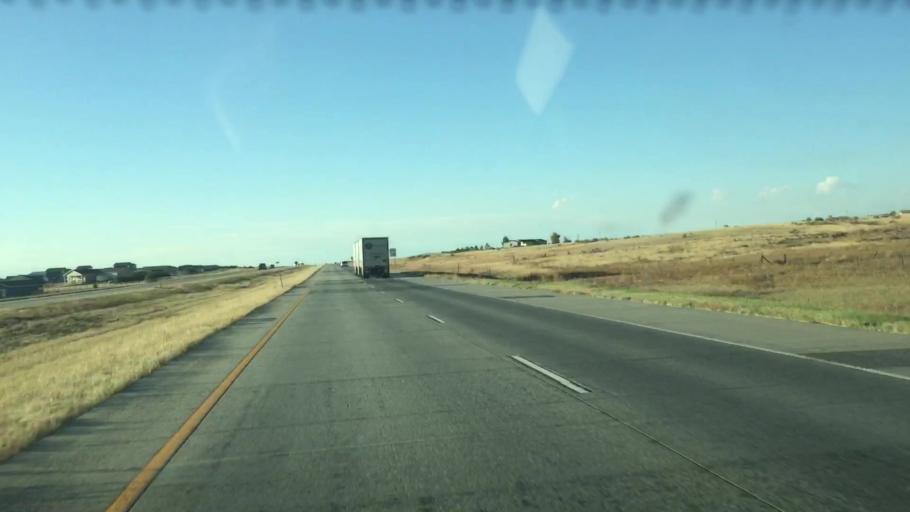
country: US
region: Colorado
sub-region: Arapahoe County
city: Byers
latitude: 39.6226
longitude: -104.0459
